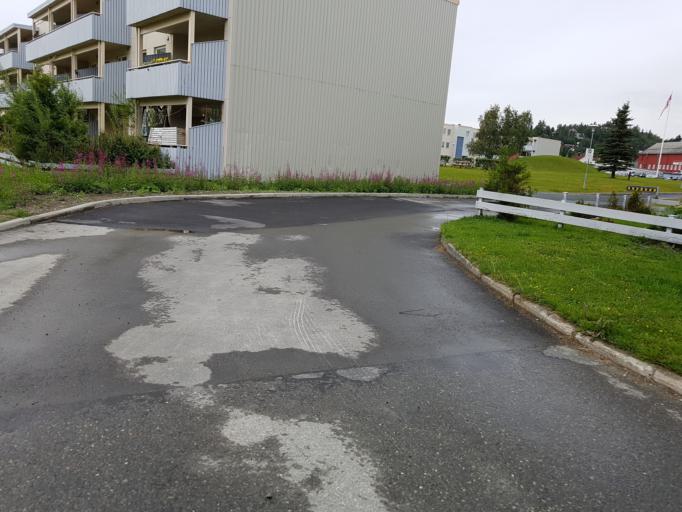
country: NO
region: Sor-Trondelag
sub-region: Trondheim
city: Trondheim
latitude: 63.3924
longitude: 10.3617
